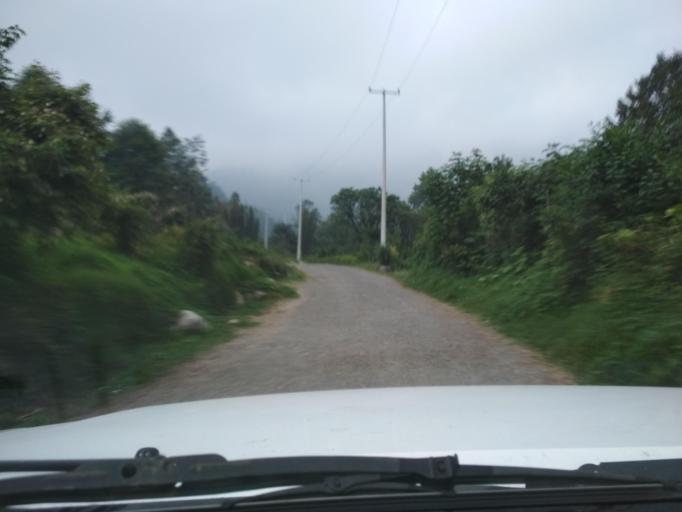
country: MX
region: Veracruz
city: La Perla
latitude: 18.9299
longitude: -97.1442
